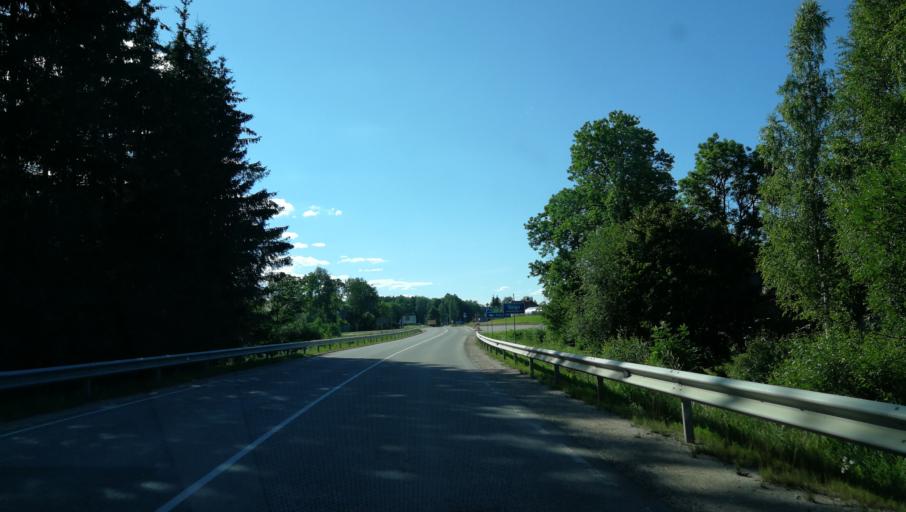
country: LV
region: Vecpiebalga
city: Vecpiebalga
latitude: 57.0573
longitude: 25.8272
